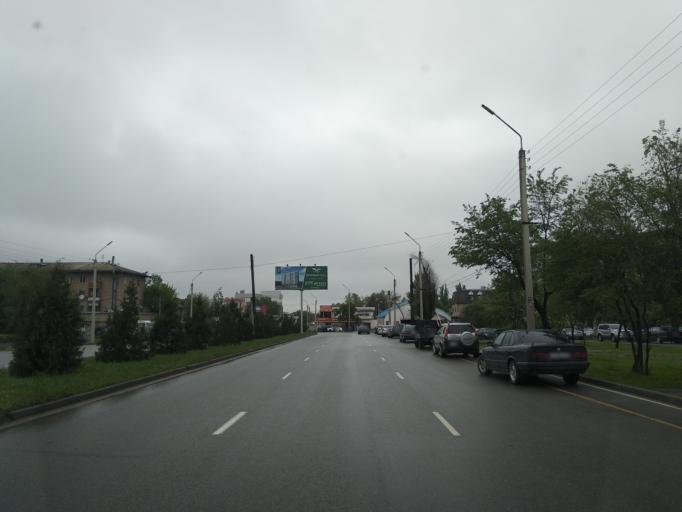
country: KG
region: Chuy
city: Bishkek
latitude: 42.8828
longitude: 74.6175
